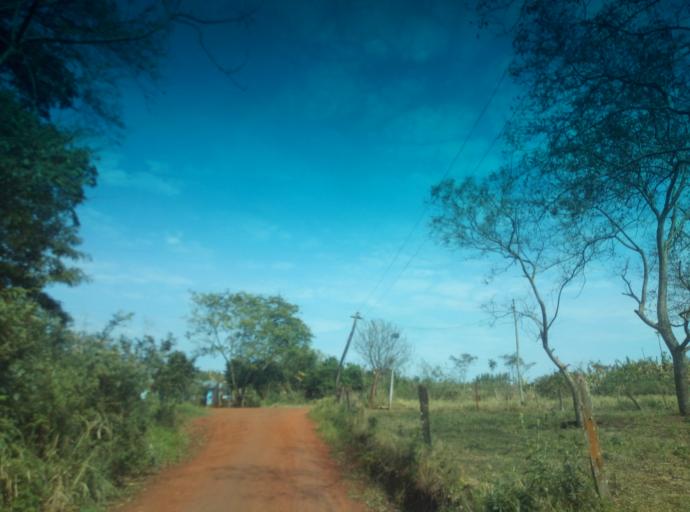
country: PY
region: Caaguazu
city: Carayao
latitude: -25.2039
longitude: -56.2528
